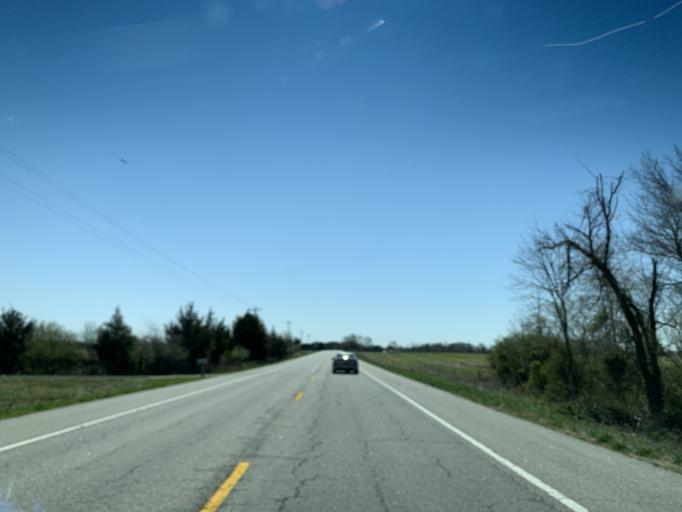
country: US
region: Maryland
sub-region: Caroline County
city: Ridgely
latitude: 38.9616
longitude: -75.9921
